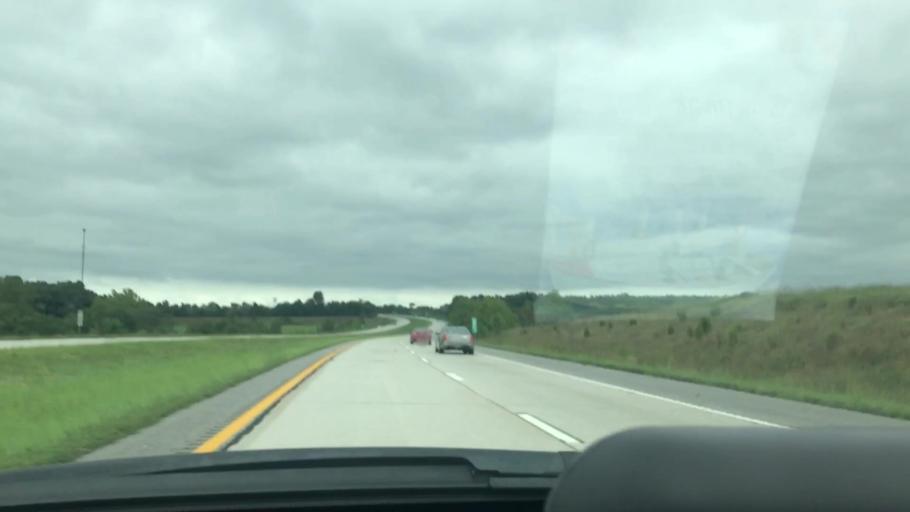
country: US
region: Missouri
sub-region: Greene County
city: Fair Grove
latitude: 37.4479
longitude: -93.1435
